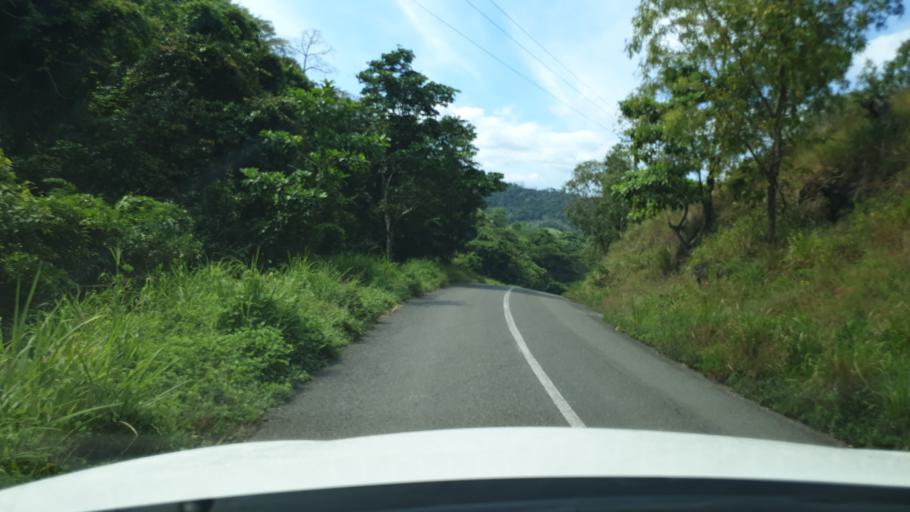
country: PG
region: Central Province
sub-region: Rigo
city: Kwikila
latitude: -9.8296
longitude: 147.5646
